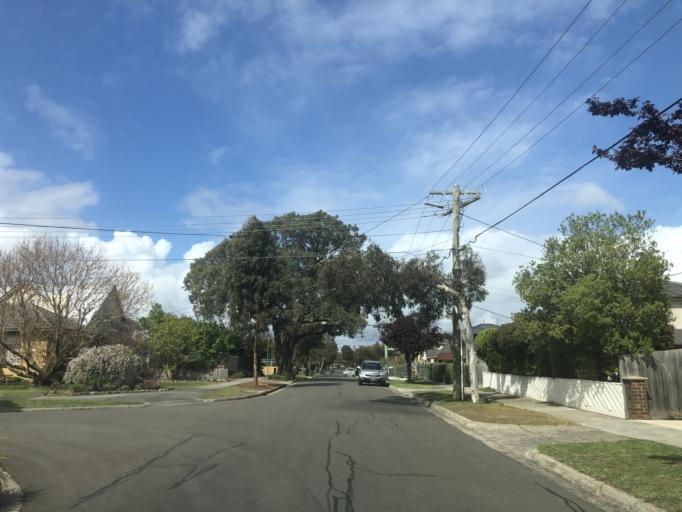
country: AU
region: Victoria
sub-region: Monash
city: Ashwood
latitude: -37.8763
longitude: 145.1158
